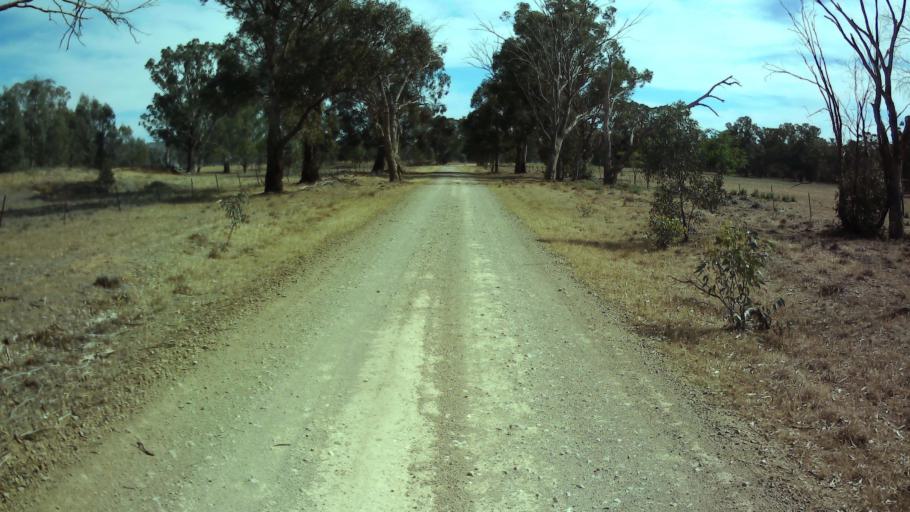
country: AU
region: New South Wales
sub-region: Weddin
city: Grenfell
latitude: -33.6935
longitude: 148.3034
